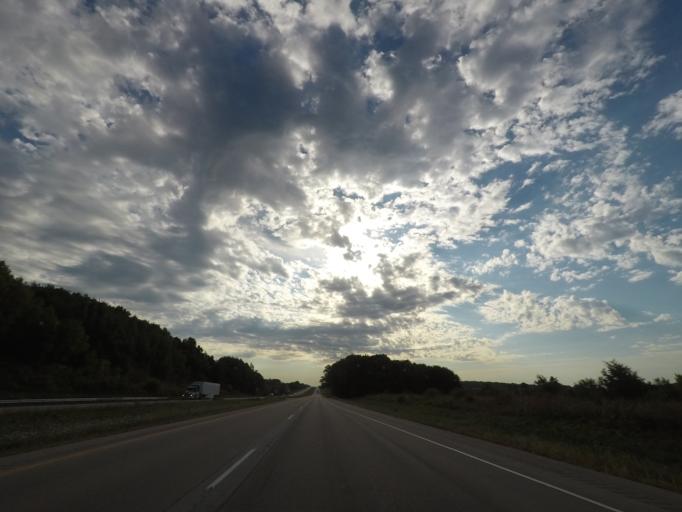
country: US
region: Wisconsin
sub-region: Dane County
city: Deerfield
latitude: 43.1091
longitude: -89.0754
